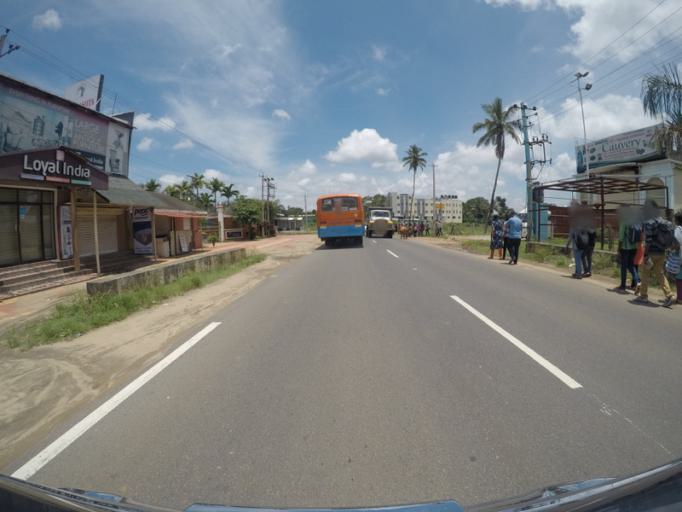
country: IN
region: Karnataka
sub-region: Kodagu
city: Kushalnagar
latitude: 12.4477
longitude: 75.9374
